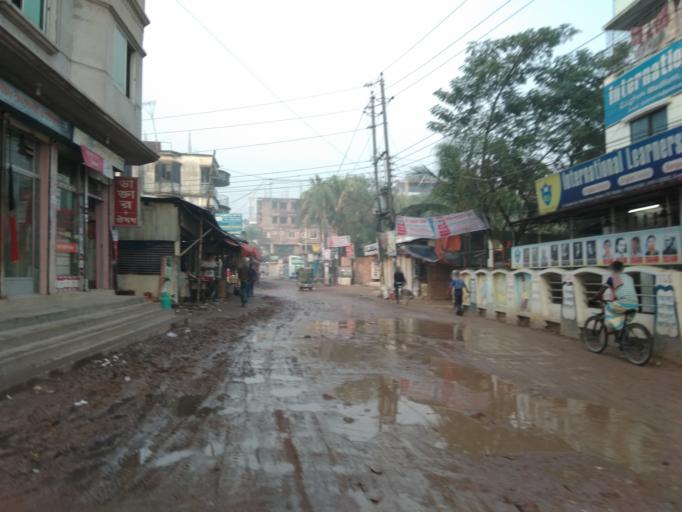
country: BD
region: Dhaka
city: Tungi
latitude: 23.8609
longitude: 90.4300
